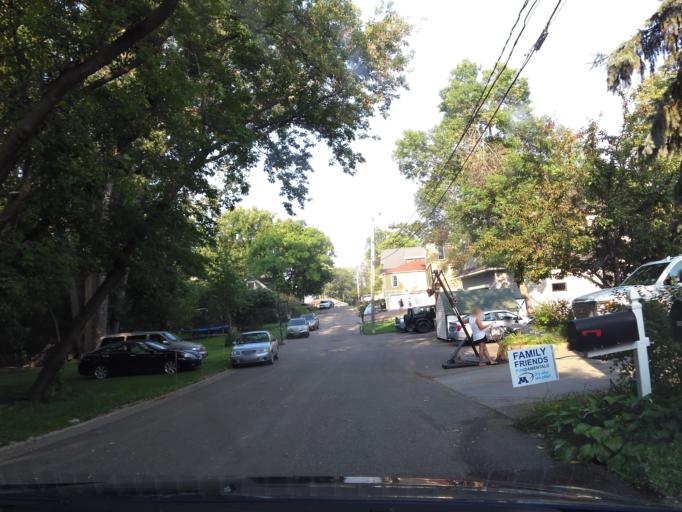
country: US
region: Minnesota
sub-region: Hennepin County
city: Shorewood
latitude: 44.8744
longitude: -93.6158
